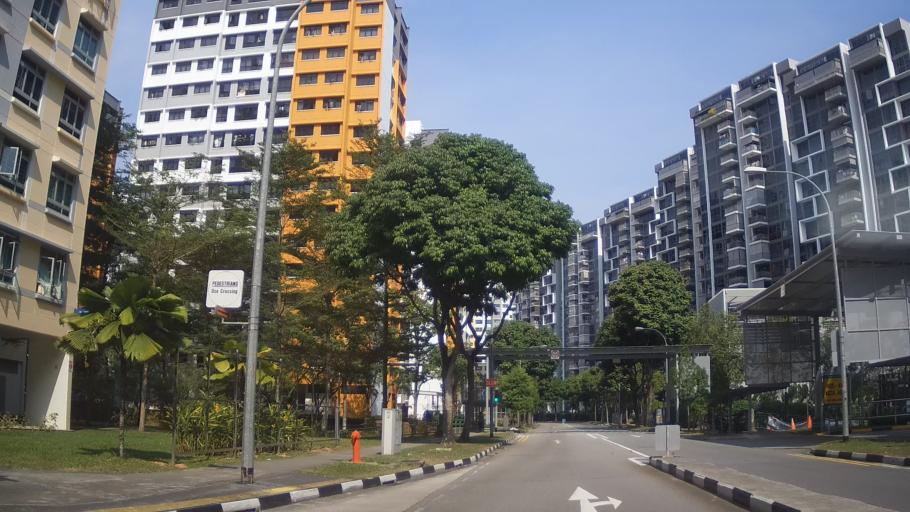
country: MY
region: Johor
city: Johor Bahru
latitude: 1.3882
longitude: 103.7712
